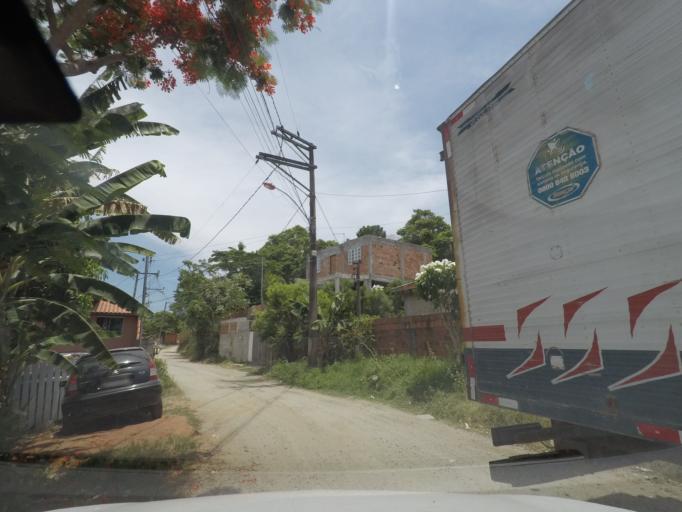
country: BR
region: Rio de Janeiro
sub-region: Marica
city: Marica
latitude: -22.9269
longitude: -42.8237
